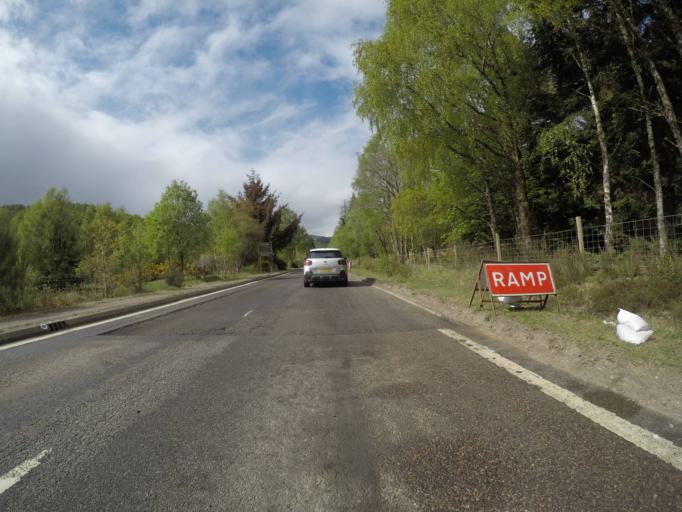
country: GB
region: Scotland
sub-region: Highland
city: Spean Bridge
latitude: 57.0673
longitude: -4.8216
